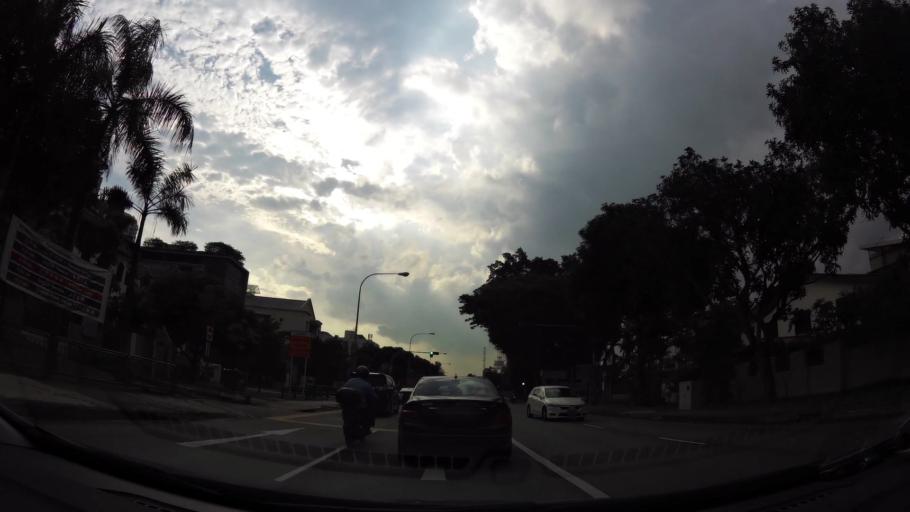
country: SG
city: Singapore
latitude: 1.3148
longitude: 103.9394
